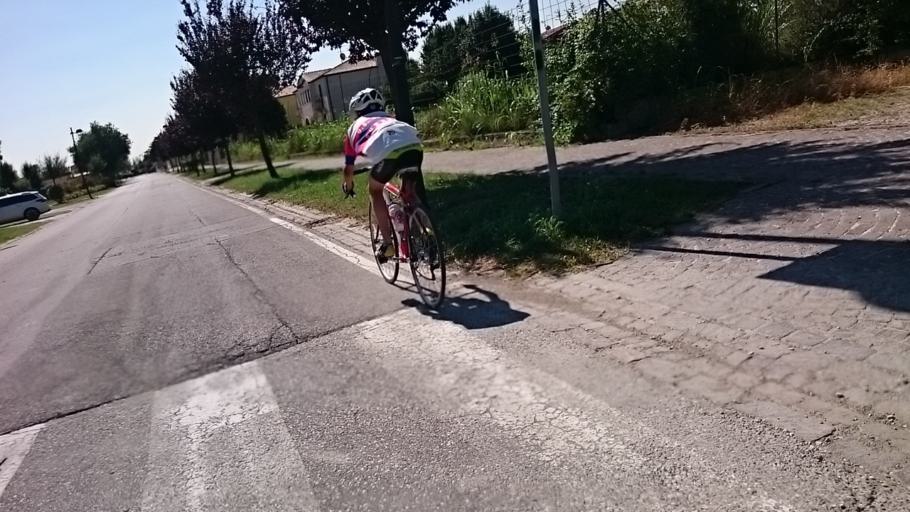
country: IT
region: Veneto
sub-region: Provincia di Padova
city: Cervarese Santa Croce
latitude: 45.4315
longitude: 11.6904
